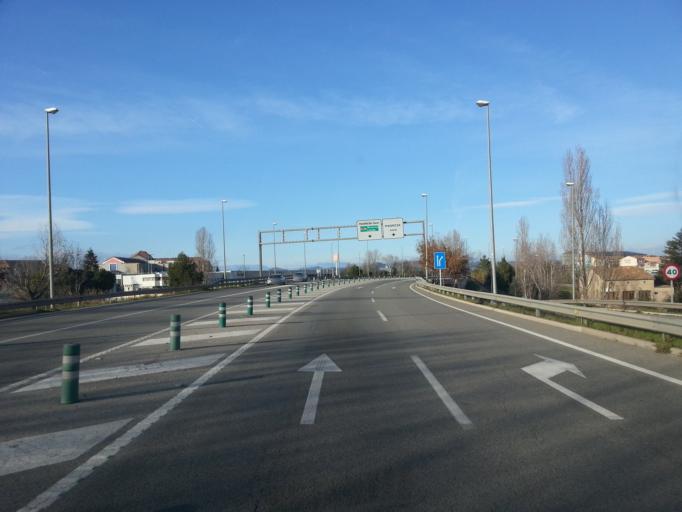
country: ES
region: Catalonia
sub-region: Provincia de Barcelona
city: Sant Fruitos de Bages
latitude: 41.7359
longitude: 1.8500
